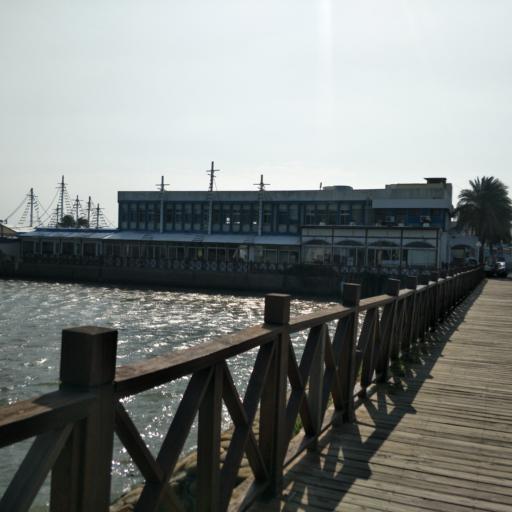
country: TW
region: Taiwan
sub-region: Hsinchu
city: Hsinchu
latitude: 24.8491
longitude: 120.9291
